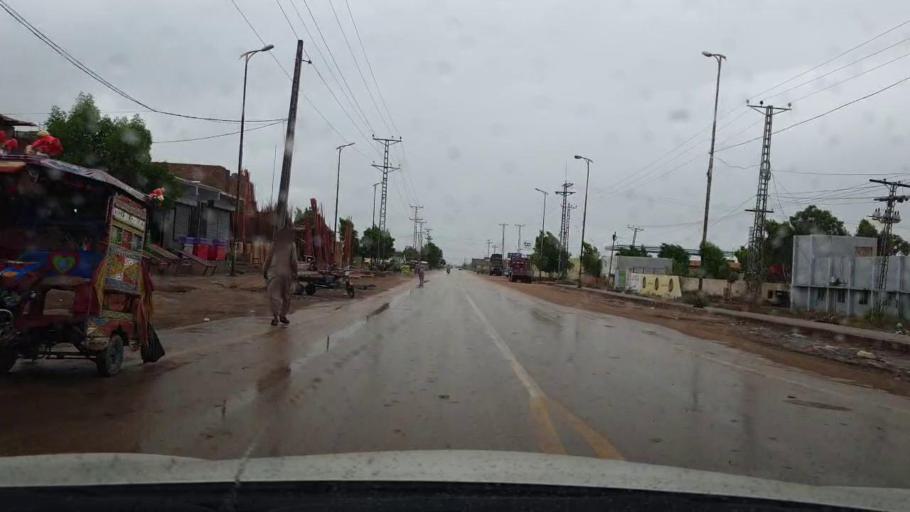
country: PK
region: Sindh
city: Kario
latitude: 24.6534
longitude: 68.5375
